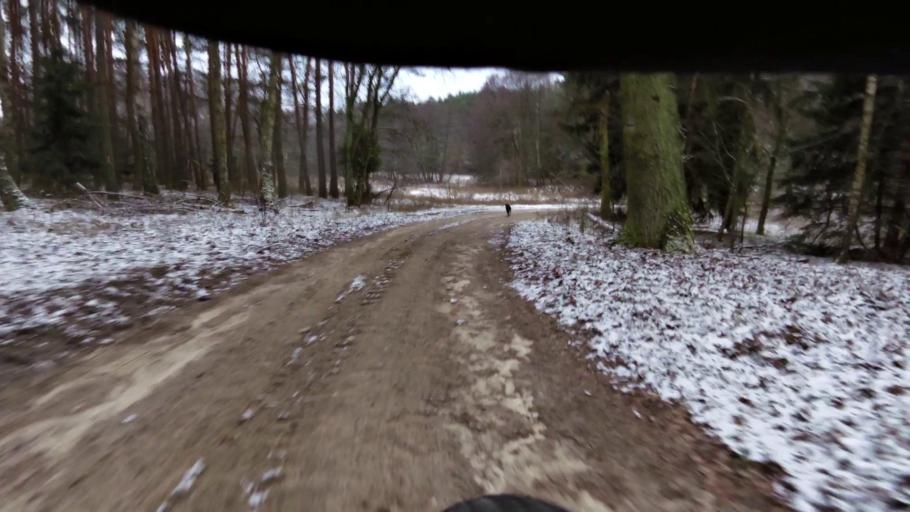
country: PL
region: West Pomeranian Voivodeship
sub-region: Powiat walecki
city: Miroslawiec
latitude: 53.2733
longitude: 16.0604
